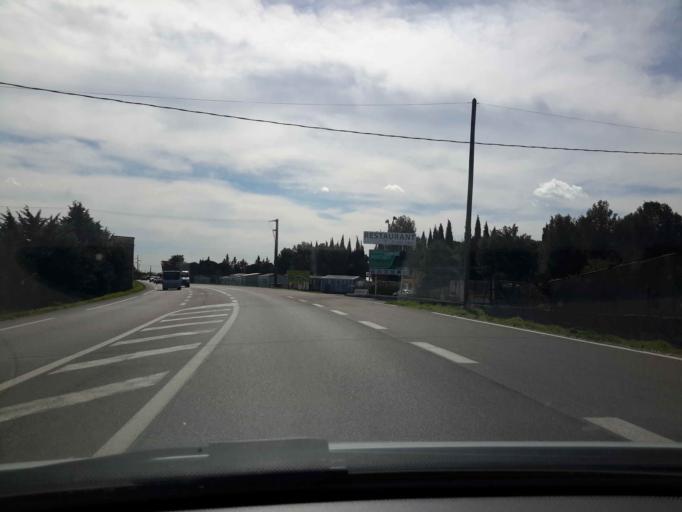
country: FR
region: Languedoc-Roussillon
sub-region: Departement du Gard
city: Le Cailar
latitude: 43.6944
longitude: 4.2524
